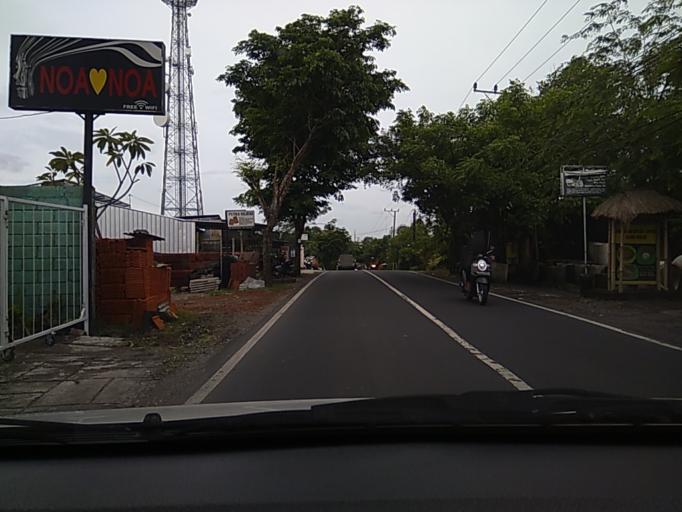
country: ID
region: Bali
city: Banjar Gunungpande
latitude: -8.6351
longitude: 115.1408
